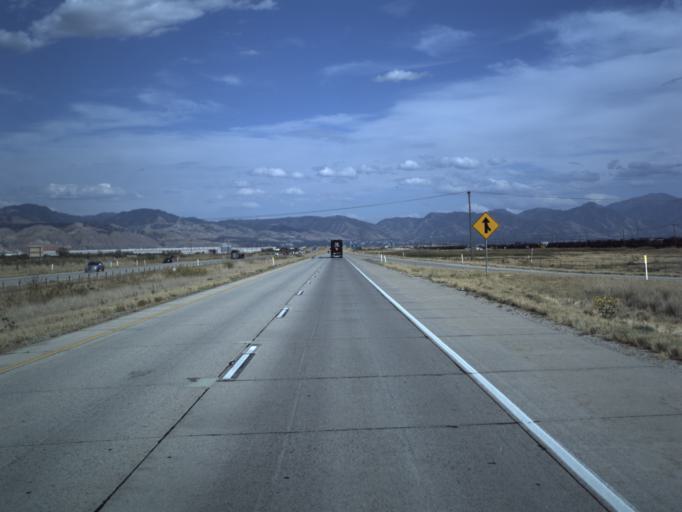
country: US
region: Utah
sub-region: Salt Lake County
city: Magna
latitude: 40.7709
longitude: -112.0589
